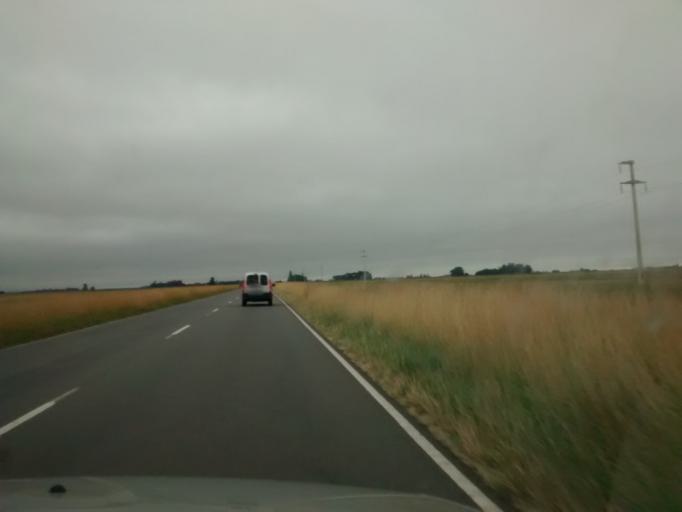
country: AR
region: Buenos Aires
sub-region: Partido de Ayacucho
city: Ayacucho
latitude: -37.0224
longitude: -58.5387
